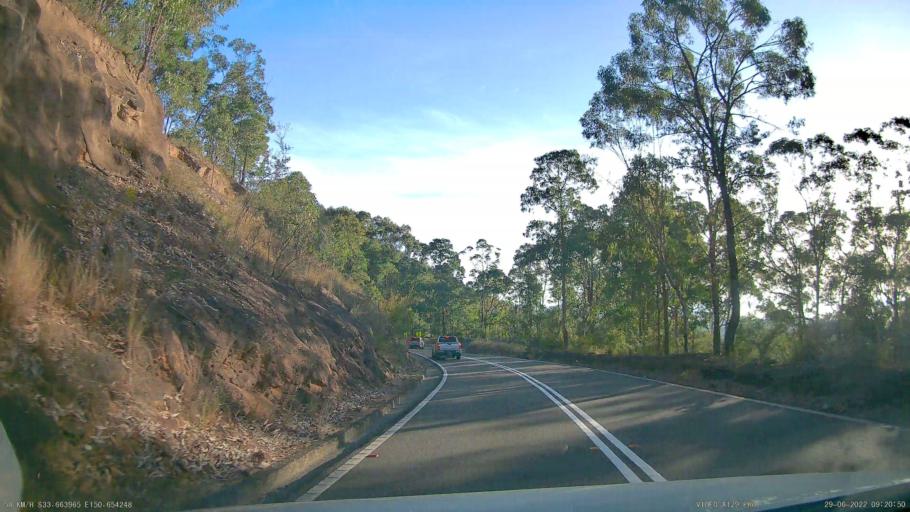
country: AU
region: New South Wales
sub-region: Penrith Municipality
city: Emu Heights
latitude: -33.6637
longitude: 150.6543
